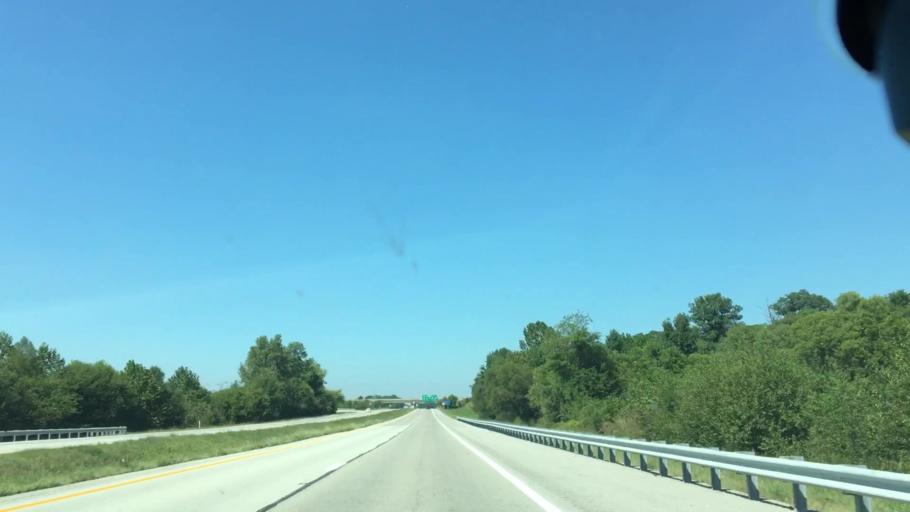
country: US
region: Kentucky
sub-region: Henderson County
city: Henderson
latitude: 37.7920
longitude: -87.5537
